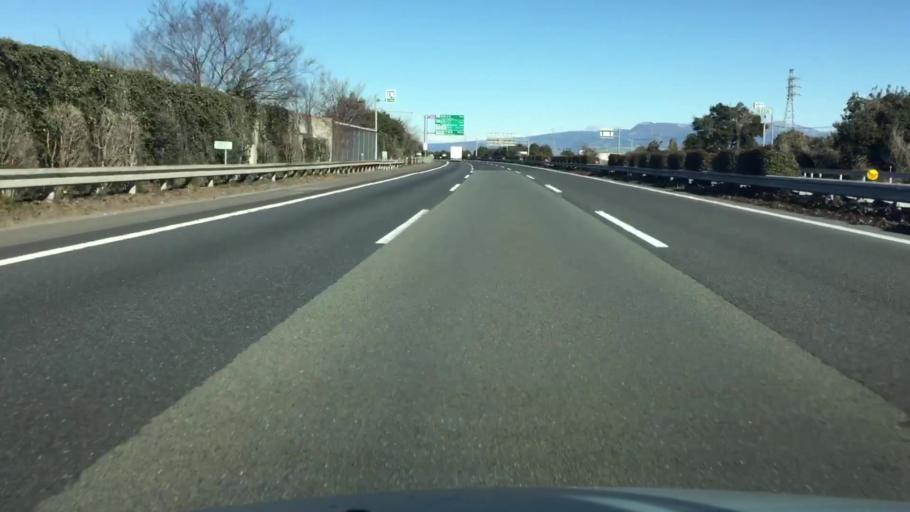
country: JP
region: Gunma
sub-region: Sawa-gun
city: Tamamura
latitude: 36.2891
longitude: 139.0980
